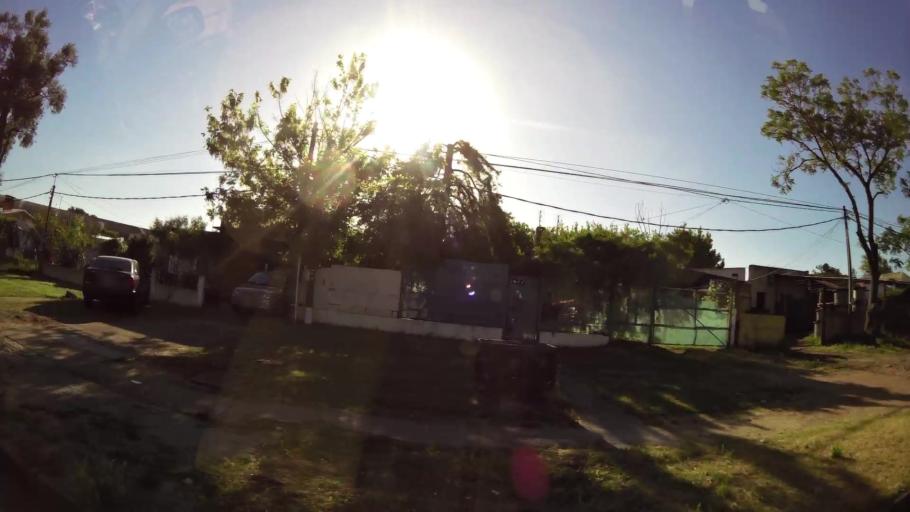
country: UY
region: Canelones
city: La Paz
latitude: -34.8302
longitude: -56.2007
